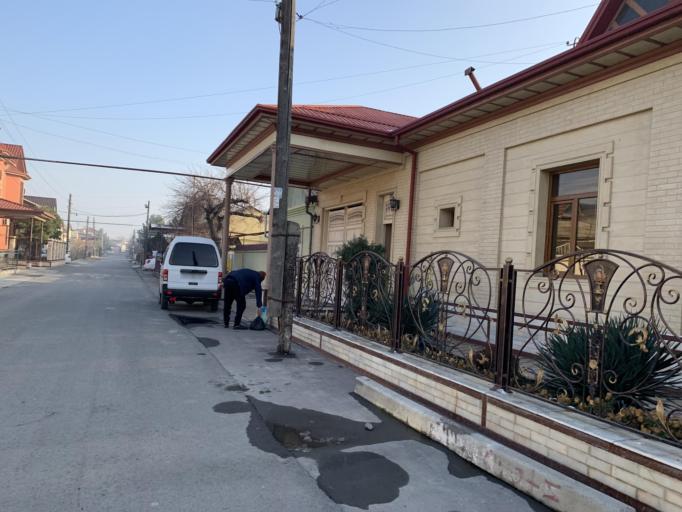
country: UZ
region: Fergana
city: Qo`qon
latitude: 40.5438
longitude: 70.9287
